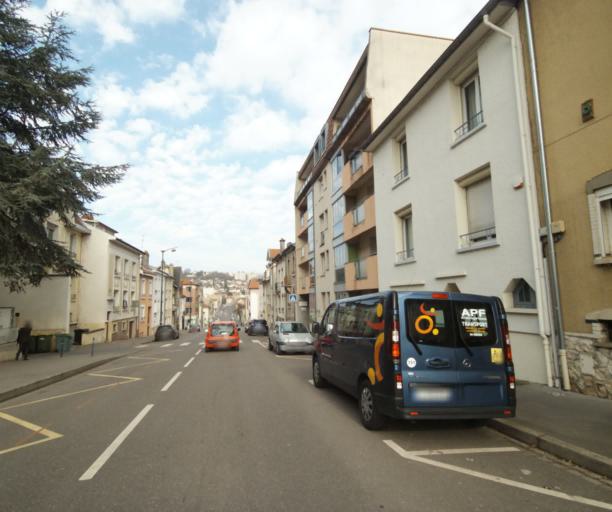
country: FR
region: Lorraine
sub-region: Departement de Meurthe-et-Moselle
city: Laxou
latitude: 48.6801
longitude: 6.1578
